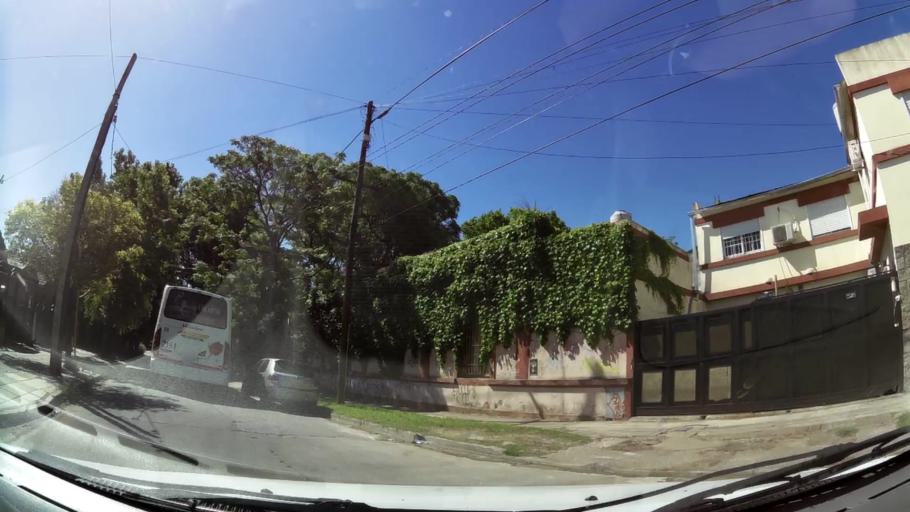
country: AR
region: Buenos Aires
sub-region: Partido de General San Martin
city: General San Martin
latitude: -34.5478
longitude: -58.5624
